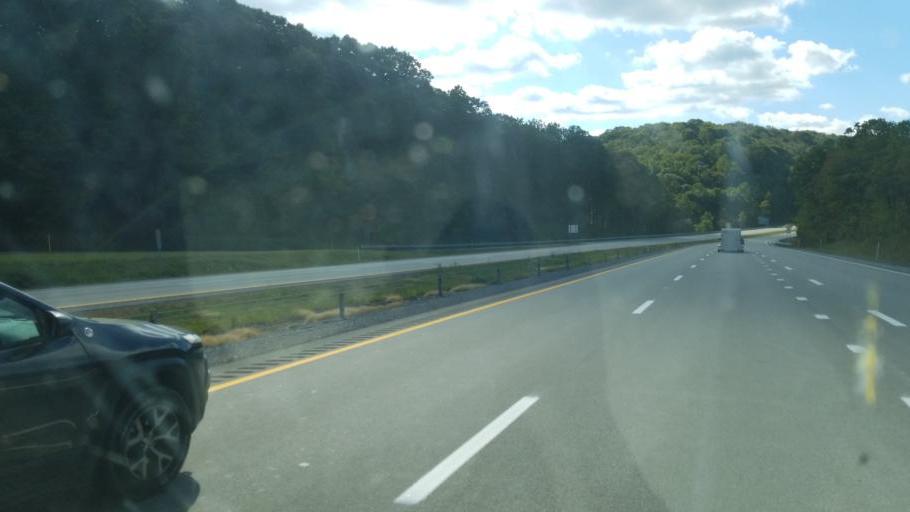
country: US
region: West Virginia
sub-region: Monongalia County
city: Cheat Lake
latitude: 39.6583
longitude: -79.7841
